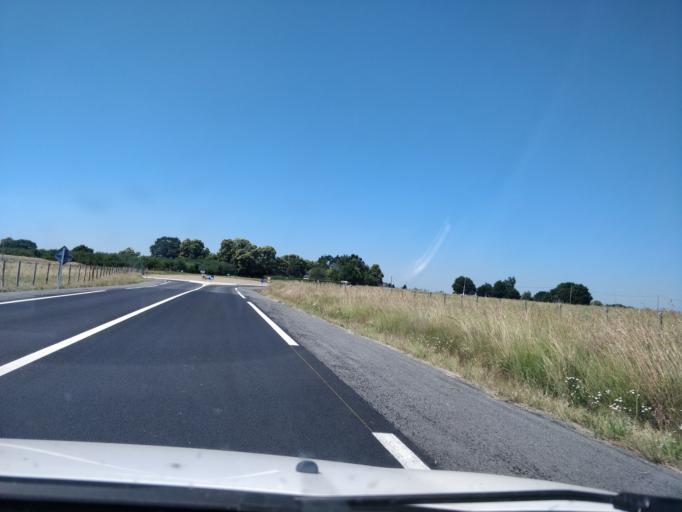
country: FR
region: Brittany
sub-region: Departement d'Ille-et-Vilaine
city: Dol-de-Bretagne
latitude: 48.5376
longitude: -1.7339
